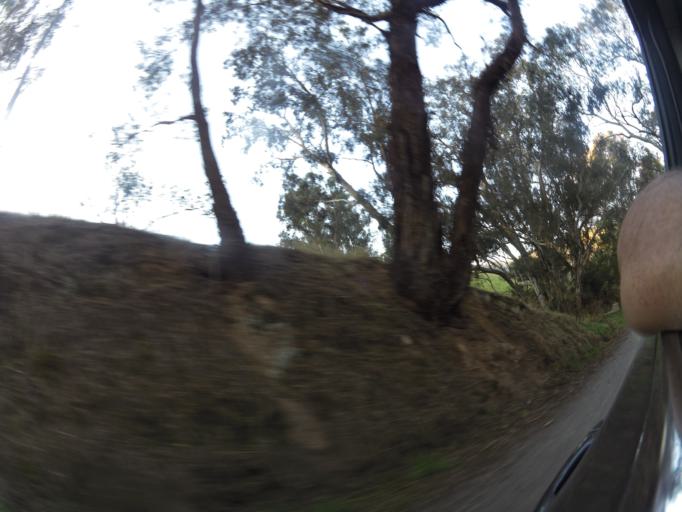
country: AU
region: Victoria
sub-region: Murrindindi
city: Alexandra
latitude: -37.1474
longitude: 145.5264
